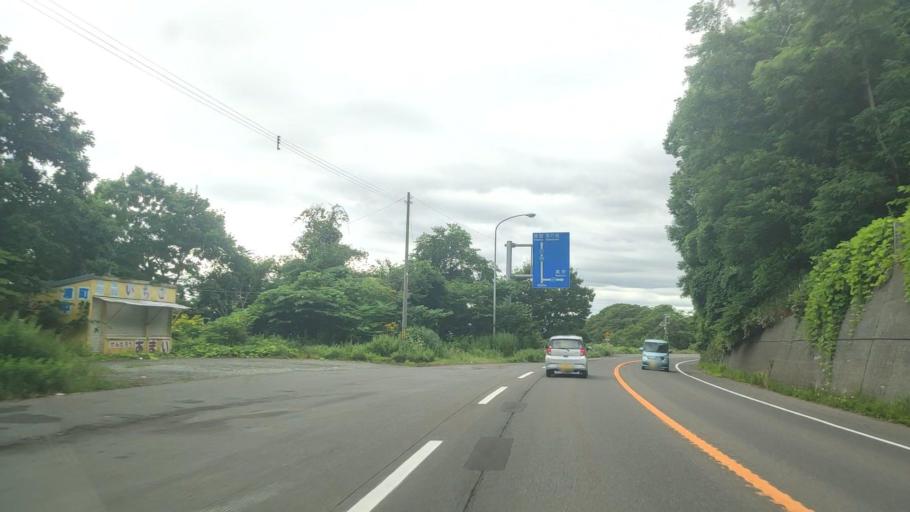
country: JP
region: Hokkaido
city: Date
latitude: 42.5746
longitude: 140.7269
